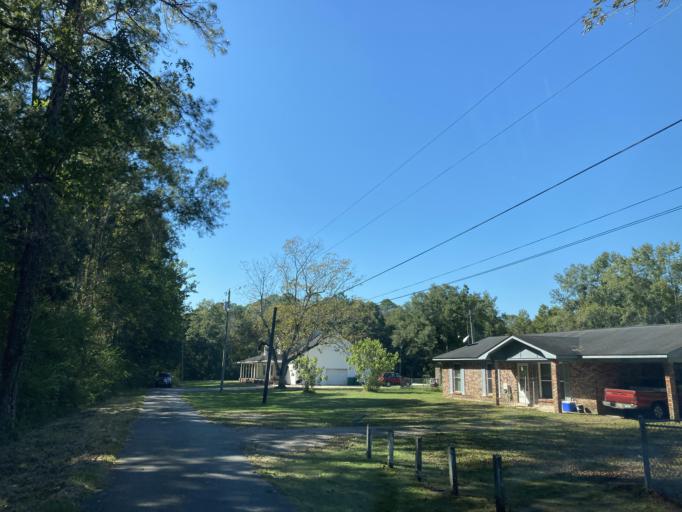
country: US
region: Mississippi
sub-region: Jackson County
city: Gulf Hills
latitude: 30.4612
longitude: -88.8458
